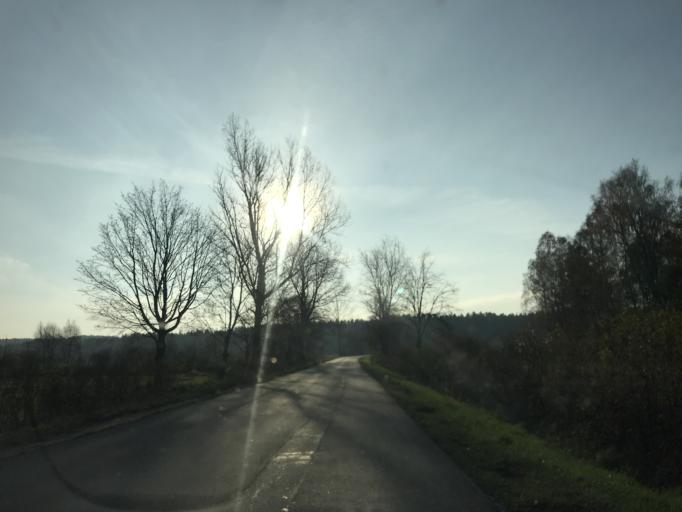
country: PL
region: Pomeranian Voivodeship
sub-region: Powiat pucki
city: Krokowa
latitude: 54.8076
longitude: 18.0979
